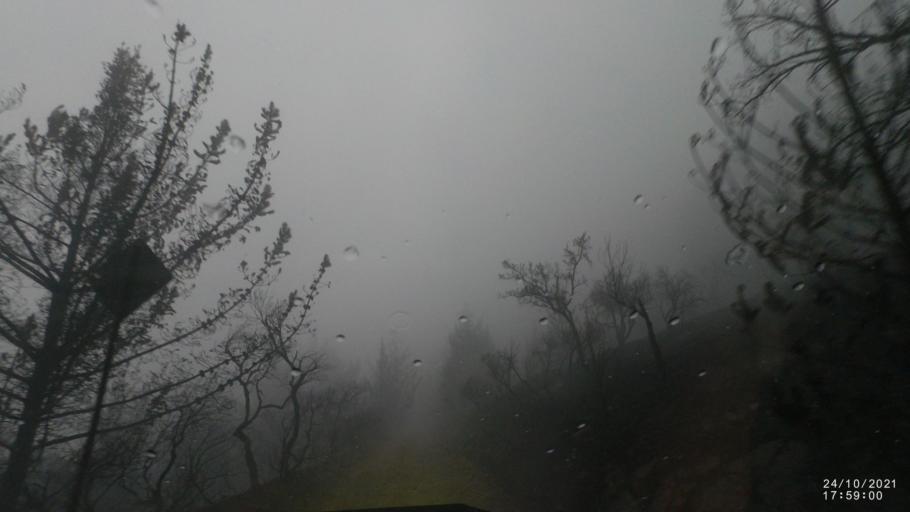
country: BO
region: Cochabamba
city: Cochabamba
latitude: -17.3253
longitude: -66.1297
